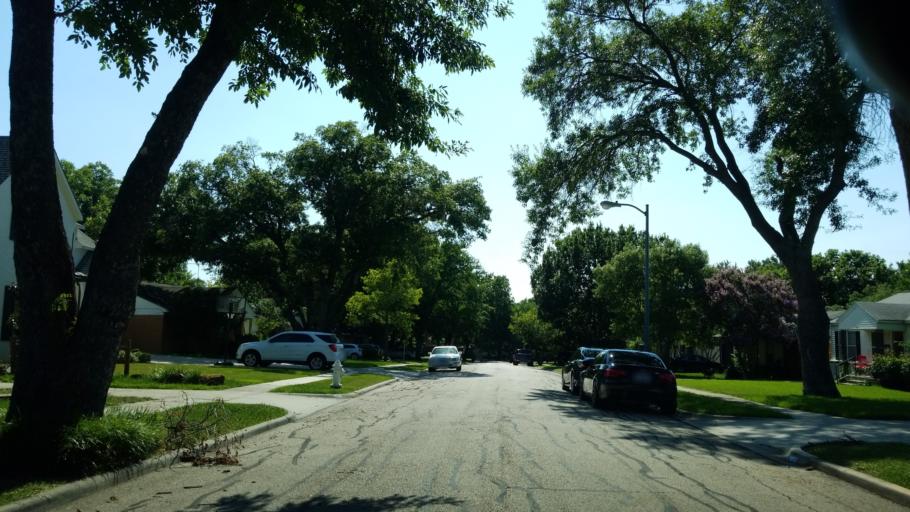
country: US
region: Texas
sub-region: Dallas County
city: Farmers Branch
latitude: 32.9203
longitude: -96.8896
